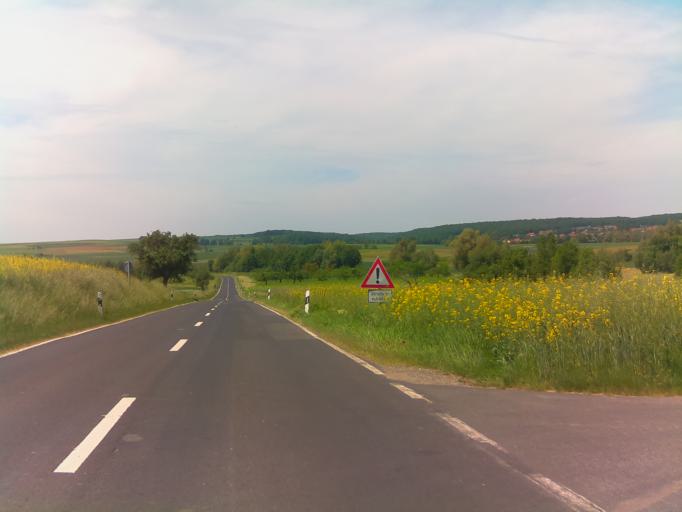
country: DE
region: Bavaria
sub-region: Regierungsbezirk Unterfranken
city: Euerbach
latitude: 50.0635
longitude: 10.1286
